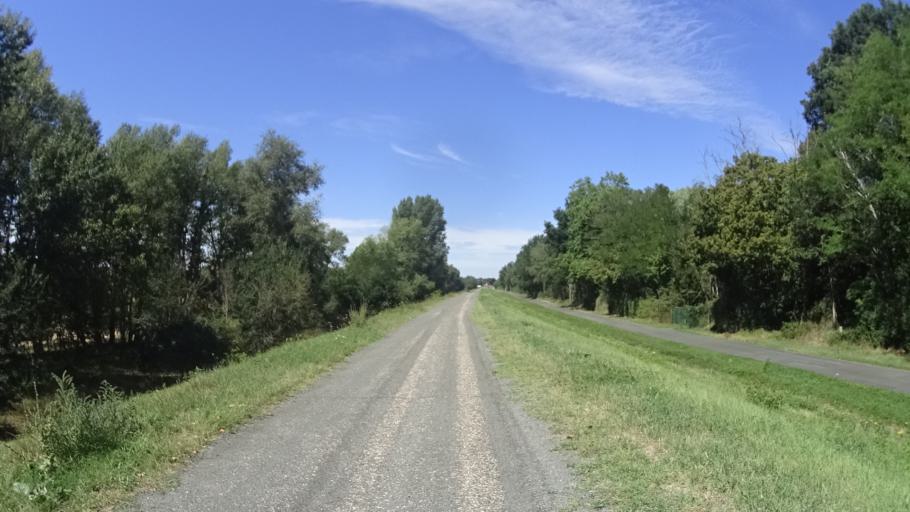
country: FR
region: Centre
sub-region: Departement du Loiret
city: Briare
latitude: 47.5942
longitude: 2.7712
